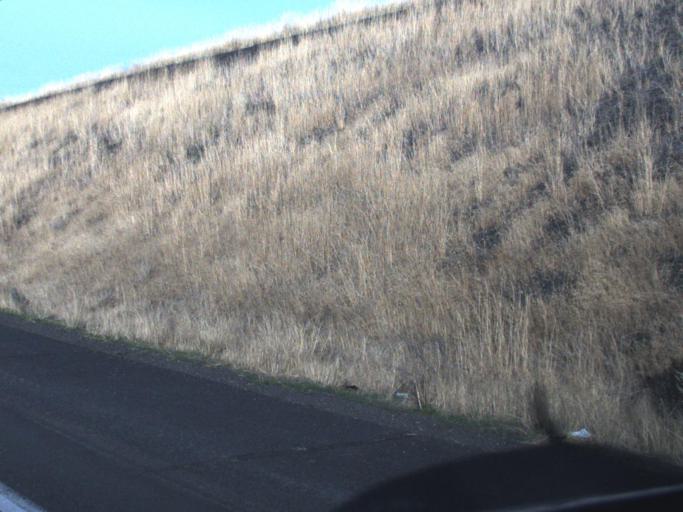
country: US
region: Oregon
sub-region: Umatilla County
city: Umatilla
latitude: 45.9687
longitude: -119.3404
